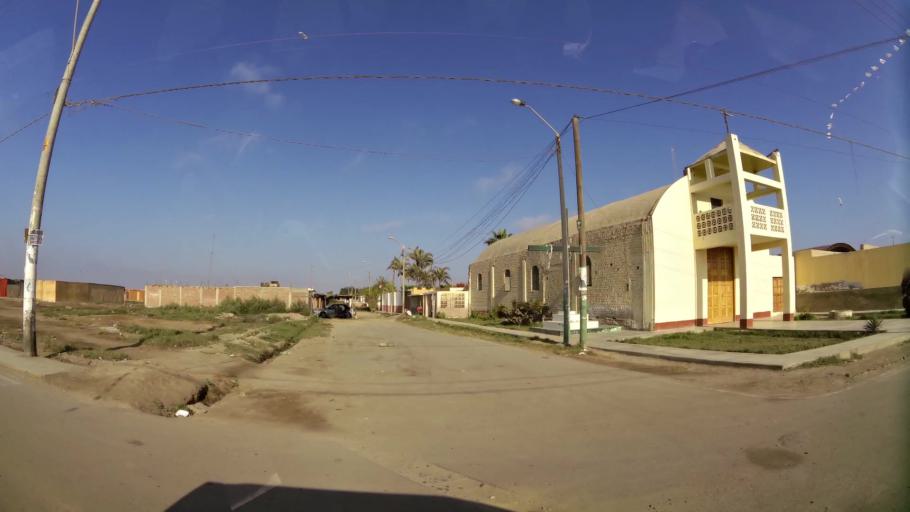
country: PE
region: Ica
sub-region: Provincia de Chincha
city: Chincha Baja
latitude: -13.4630
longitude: -76.1860
